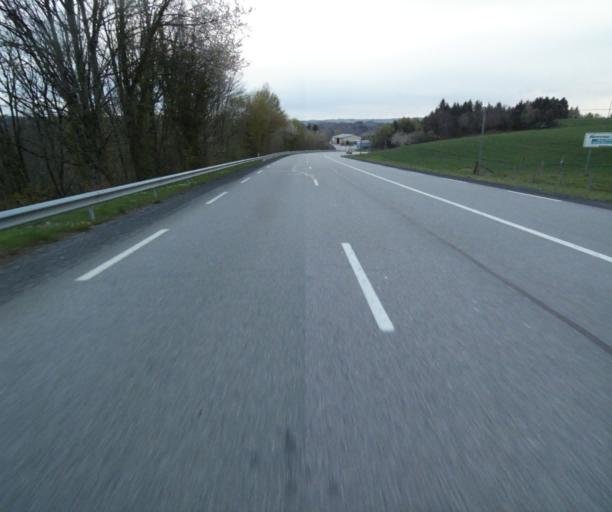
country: FR
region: Limousin
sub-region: Departement de la Correze
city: Naves
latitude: 45.2997
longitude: 1.8150
